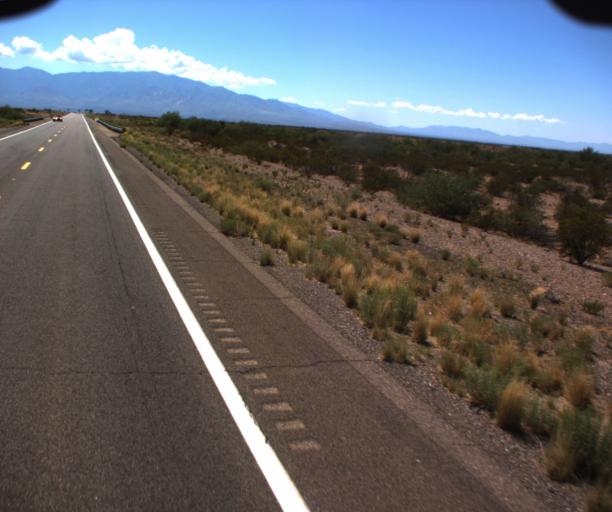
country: US
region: Arizona
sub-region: Graham County
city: Safford
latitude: 32.7946
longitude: -109.5431
